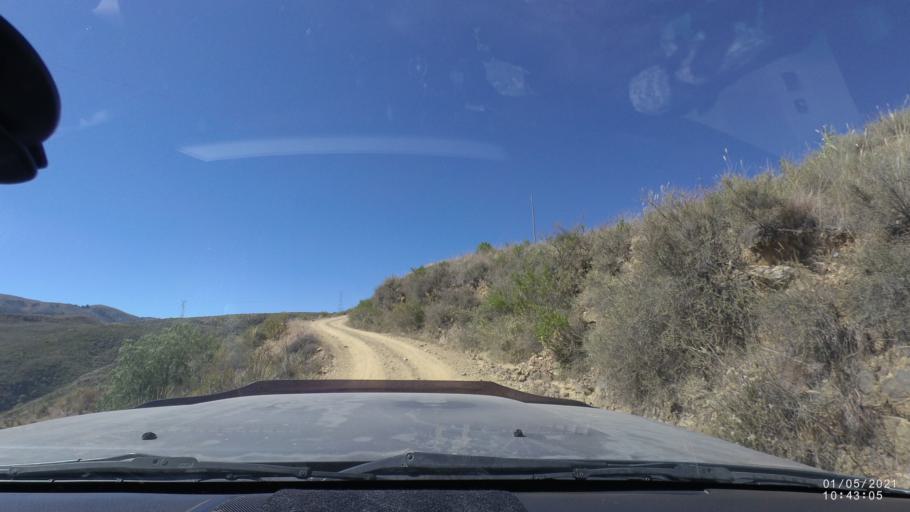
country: BO
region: Cochabamba
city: Capinota
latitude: -17.6144
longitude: -66.1754
